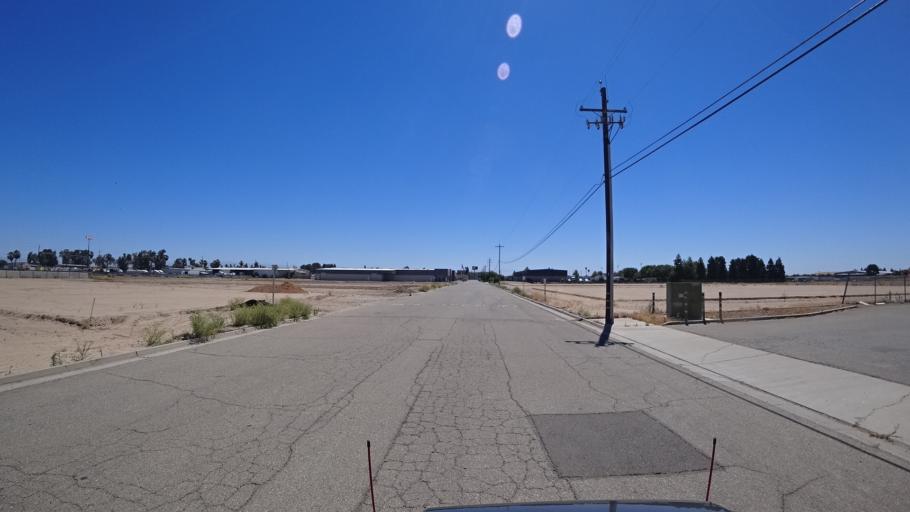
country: US
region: California
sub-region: Fresno County
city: Fresno
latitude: 36.7042
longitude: -119.7792
